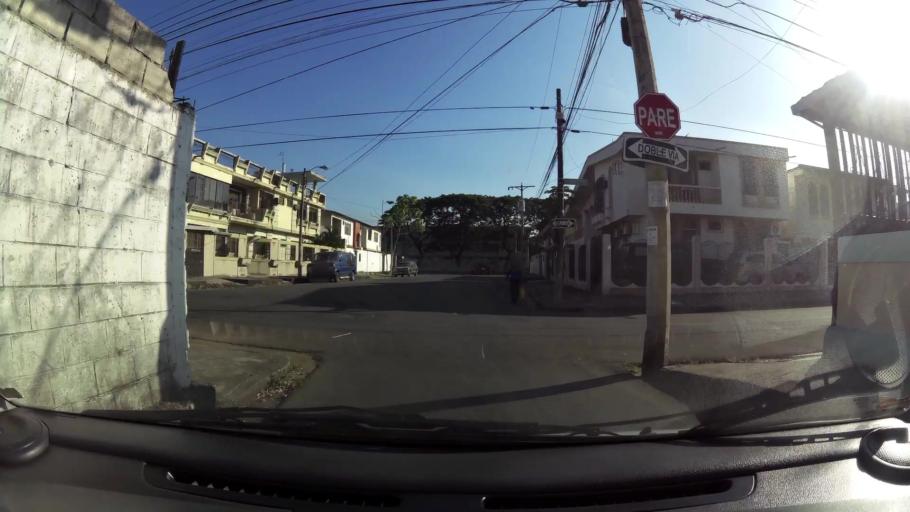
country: EC
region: Guayas
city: Eloy Alfaro
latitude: -2.1672
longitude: -79.8844
